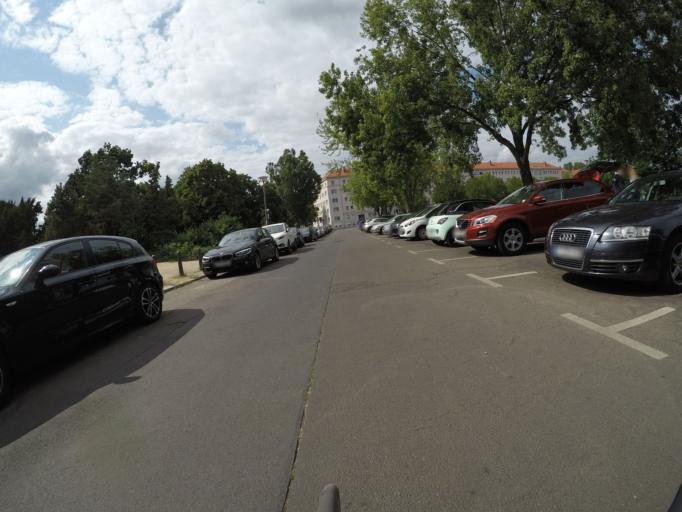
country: DE
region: Berlin
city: Prenzlauer Berg Bezirk
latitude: 52.5289
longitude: 13.4383
